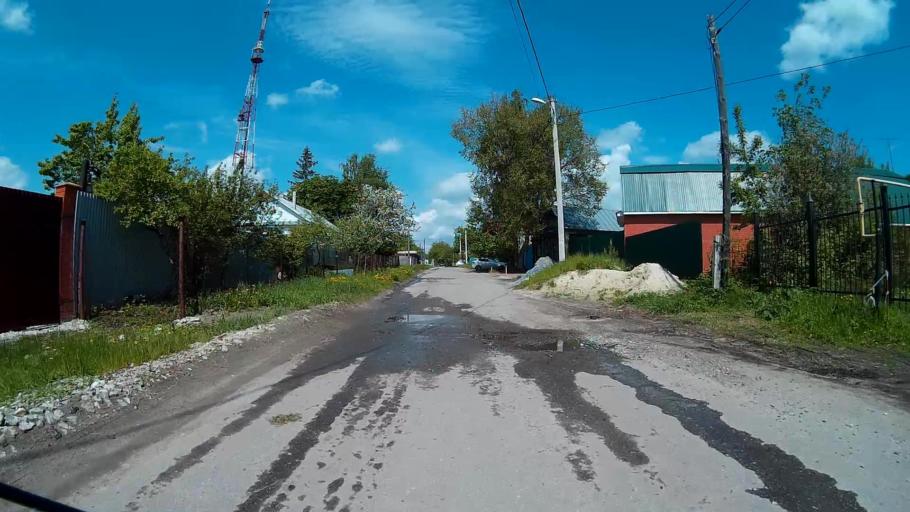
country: RU
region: Ulyanovsk
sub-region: Ulyanovskiy Rayon
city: Ulyanovsk
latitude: 54.3398
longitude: 48.3838
